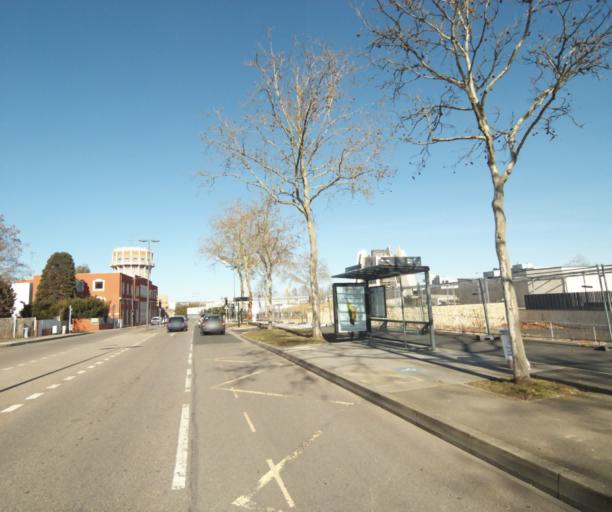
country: FR
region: Lorraine
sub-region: Departement de Meurthe-et-Moselle
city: Vandoeuvre-les-Nancy
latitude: 48.6669
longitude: 6.1769
